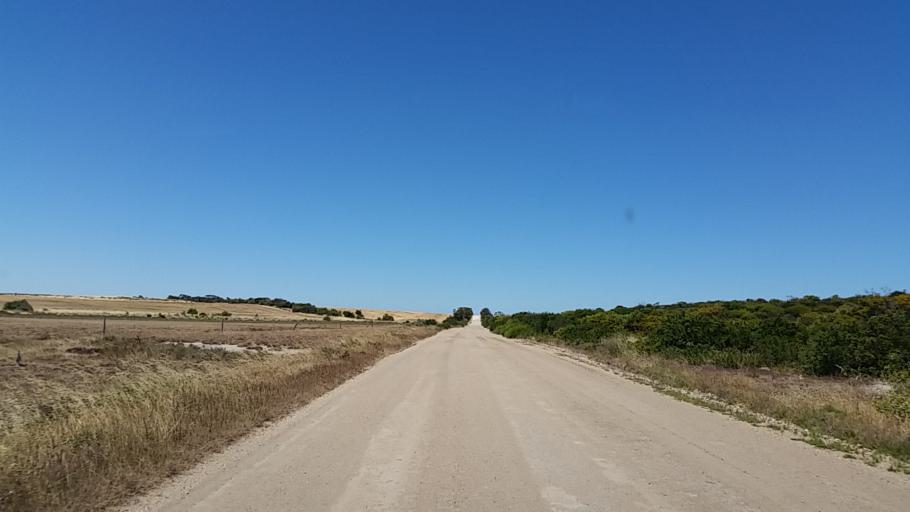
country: AU
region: South Australia
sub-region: Yorke Peninsula
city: Honiton
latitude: -35.0941
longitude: 137.4275
